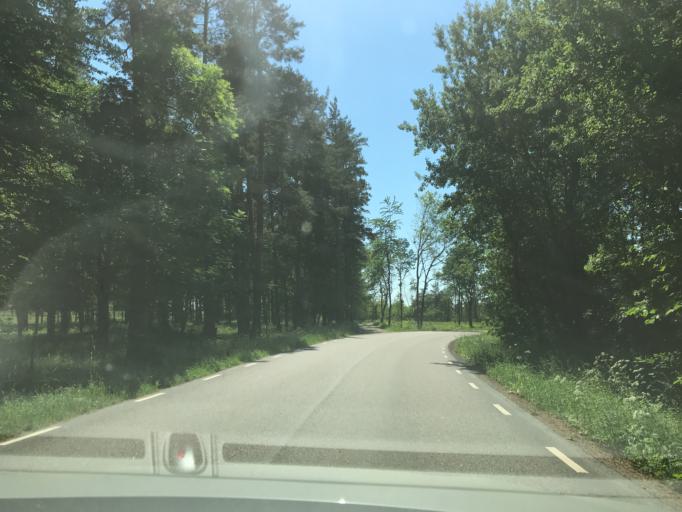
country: SE
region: Vaestra Goetaland
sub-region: Gotene Kommun
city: Kallby
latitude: 58.5283
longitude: 13.3229
